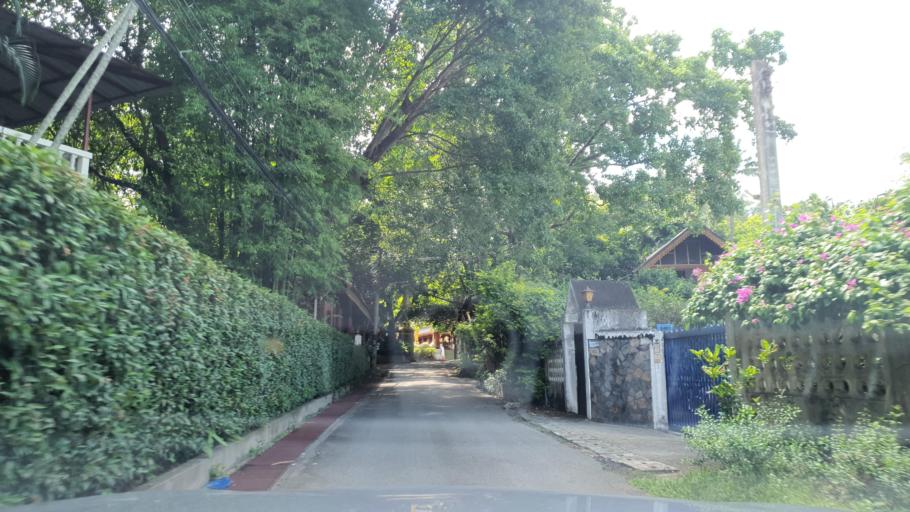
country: TH
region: Chiang Mai
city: Chiang Mai
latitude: 18.7743
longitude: 98.9496
